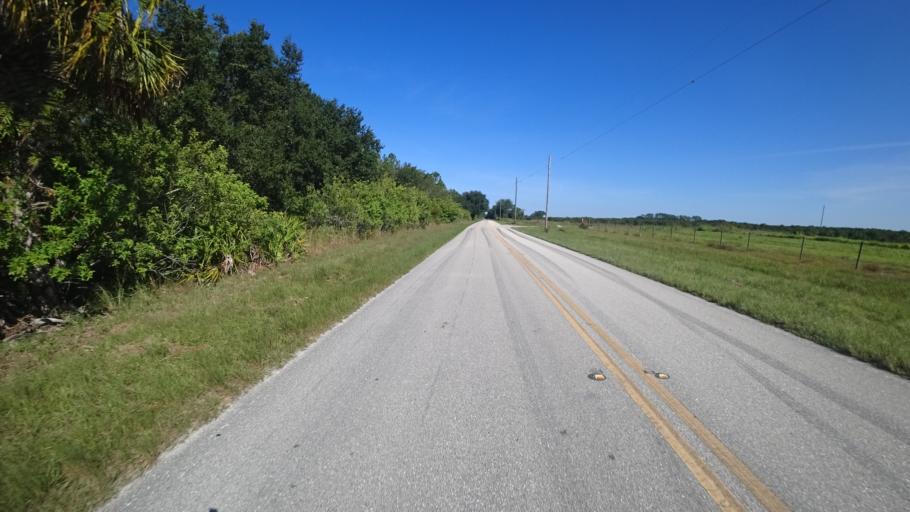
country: US
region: Florida
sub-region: Hillsborough County
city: Wimauma
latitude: 27.6213
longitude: -82.2926
